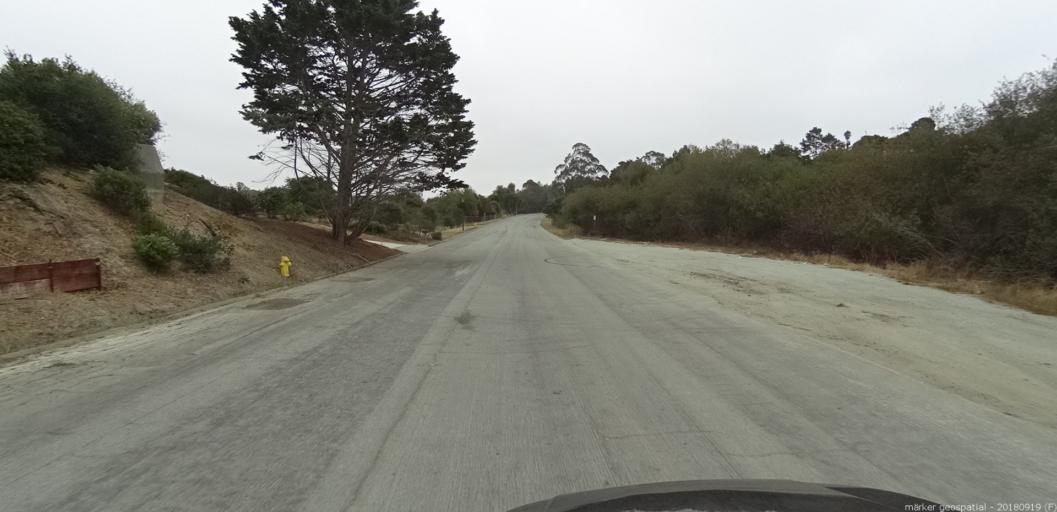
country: US
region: California
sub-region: Monterey County
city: Castroville
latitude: 36.7794
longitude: -121.7177
